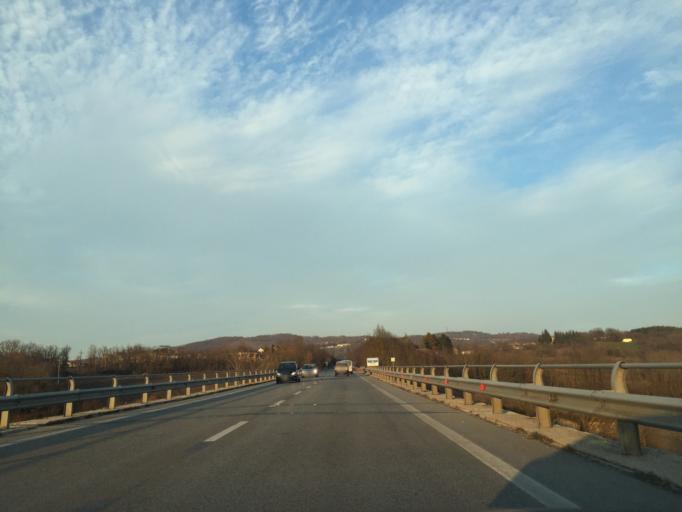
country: IT
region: Molise
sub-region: Provincia di Campobasso
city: Vinchiaturo
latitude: 41.4882
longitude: 14.5959
